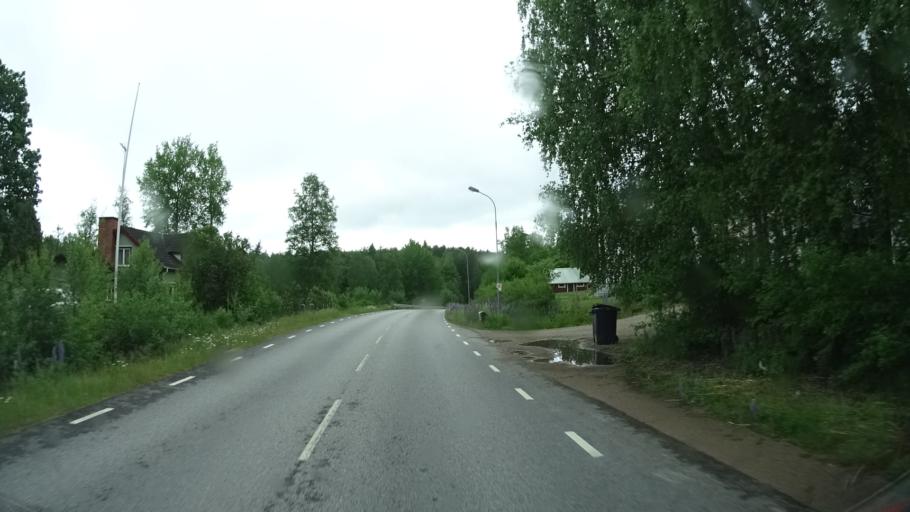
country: SE
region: Joenkoeping
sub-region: Eksjo Kommun
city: Mariannelund
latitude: 57.6845
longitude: 15.6216
